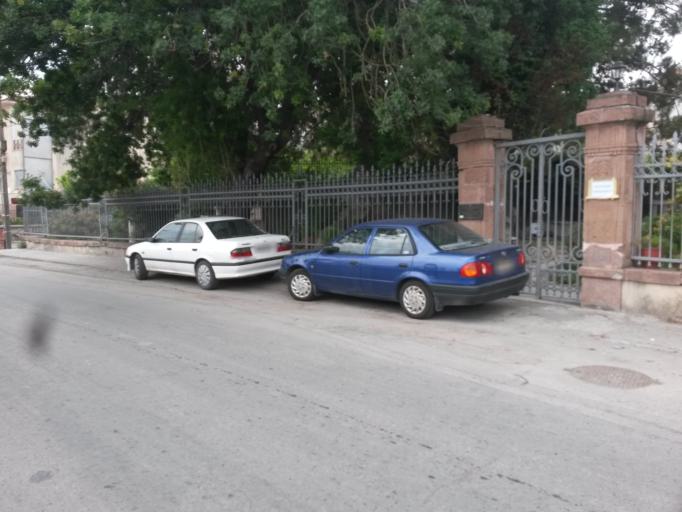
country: GR
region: North Aegean
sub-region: Nomos Lesvou
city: Mytilini
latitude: 39.1054
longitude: 26.5613
